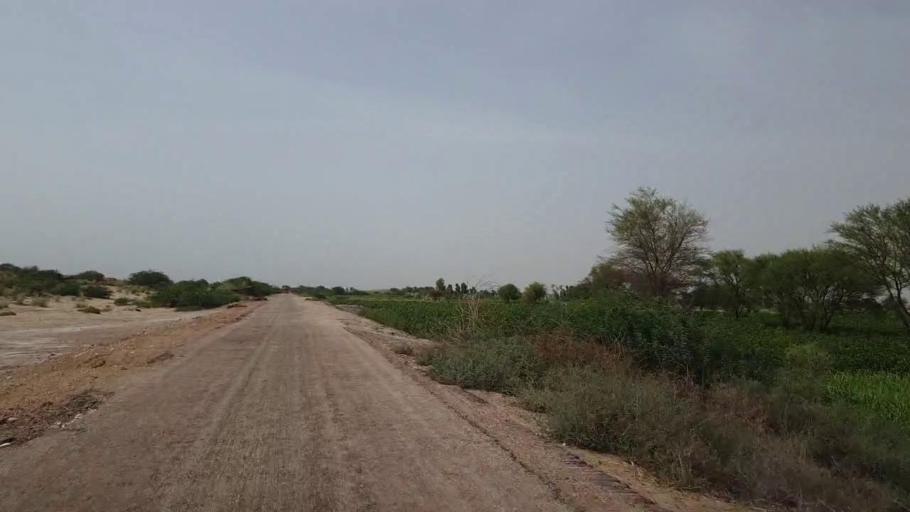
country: PK
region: Sindh
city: Bandhi
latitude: 26.5469
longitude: 68.3850
